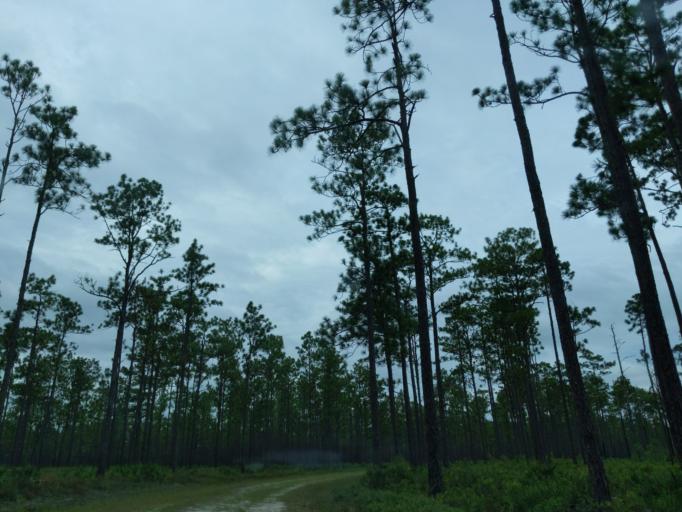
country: US
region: Florida
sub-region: Gadsden County
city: Midway
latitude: 30.3590
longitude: -84.4875
